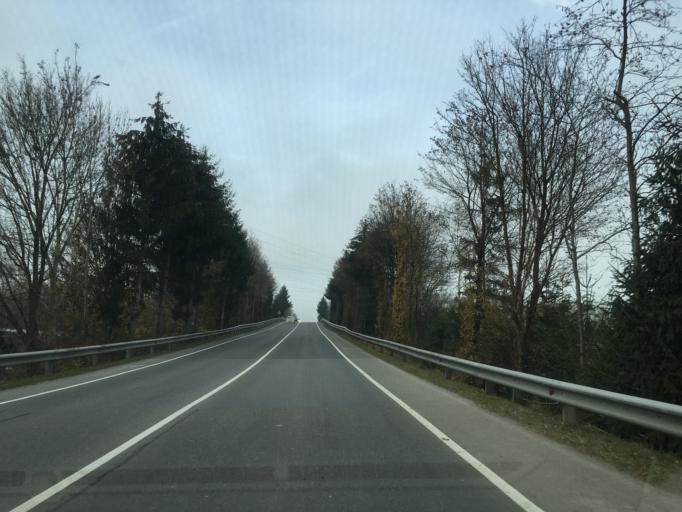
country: AT
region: Vorarlberg
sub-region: Politischer Bezirk Dornbirn
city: Hohenems
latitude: 47.3902
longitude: 9.6839
